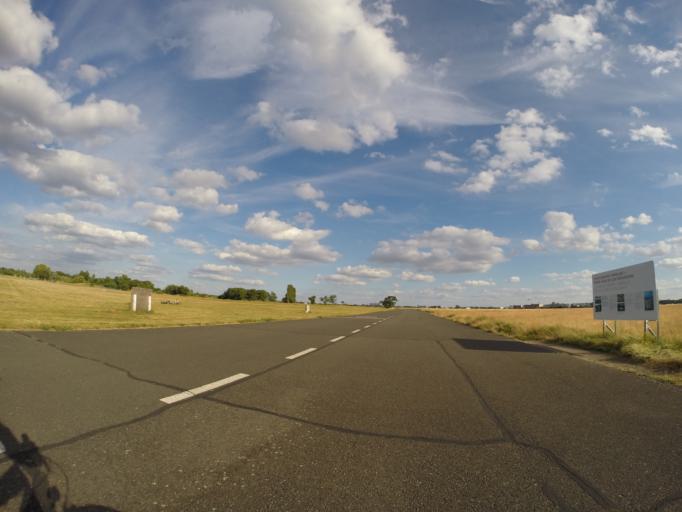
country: DE
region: Berlin
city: Tempelhof Bezirk
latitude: 52.4799
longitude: 13.3976
